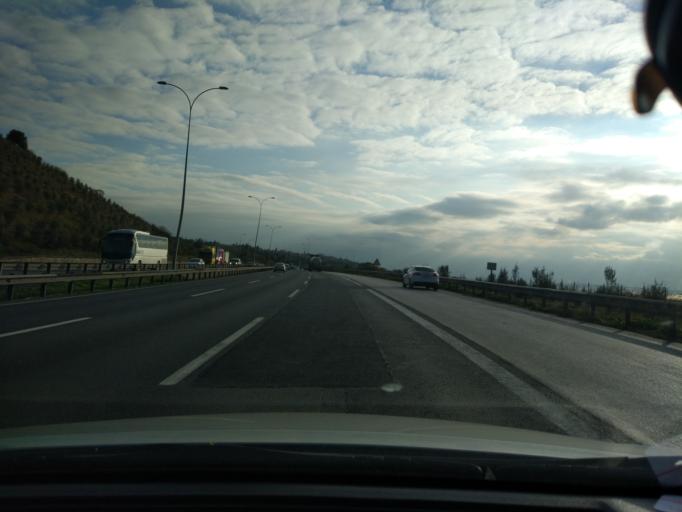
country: TR
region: Kocaeli
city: Tavsancil
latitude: 40.7736
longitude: 29.5522
